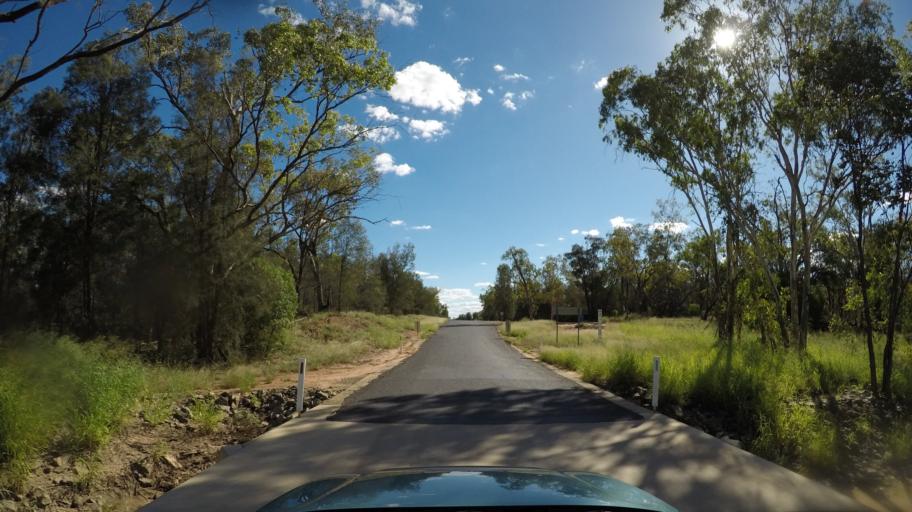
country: AU
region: Queensland
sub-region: Goondiwindi
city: Goondiwindi
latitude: -28.1750
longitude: 150.4689
